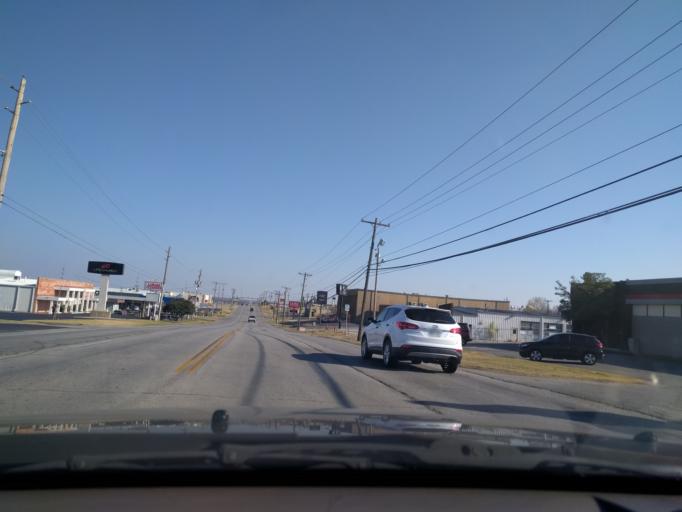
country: US
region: Oklahoma
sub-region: Tulsa County
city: Tulsa
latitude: 36.1043
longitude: -95.8991
